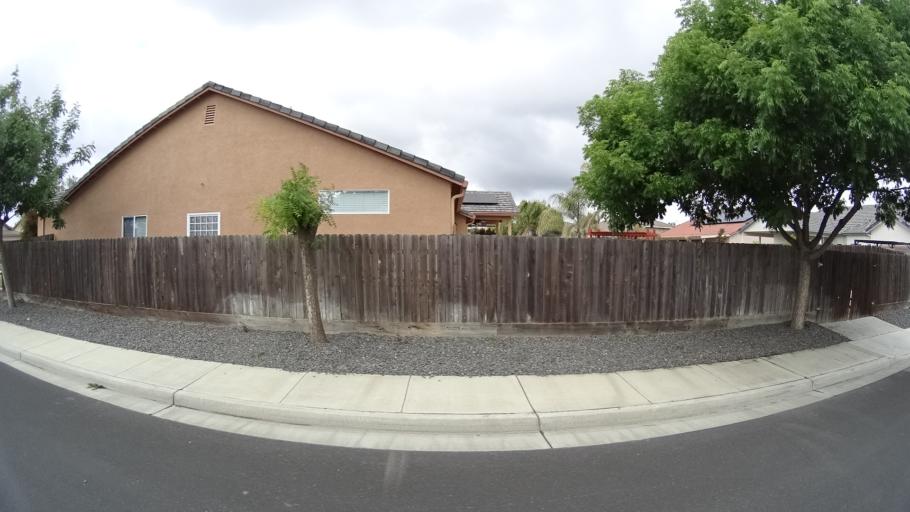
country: US
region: California
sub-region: Kings County
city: Hanford
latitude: 36.3490
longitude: -119.6685
